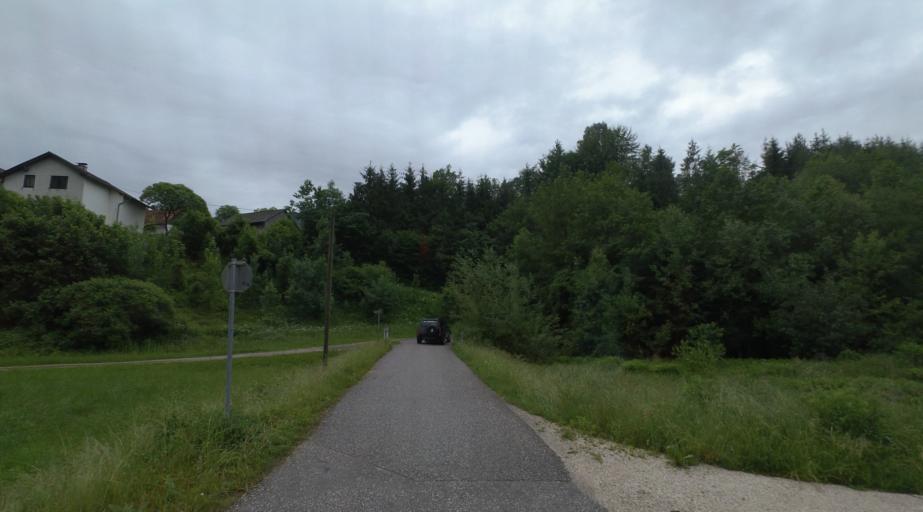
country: AT
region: Upper Austria
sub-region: Politischer Bezirk Kirchdorf an der Krems
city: Gruenburg
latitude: 47.8939
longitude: 14.2800
